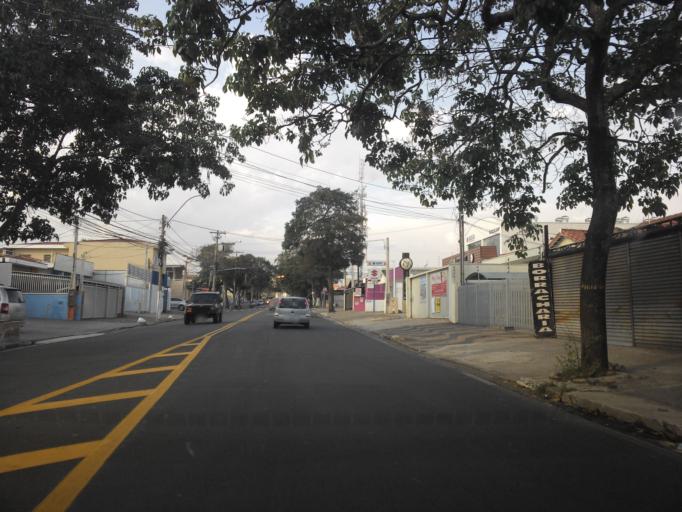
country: BR
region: Sao Paulo
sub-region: Campinas
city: Campinas
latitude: -22.8927
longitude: -47.0800
